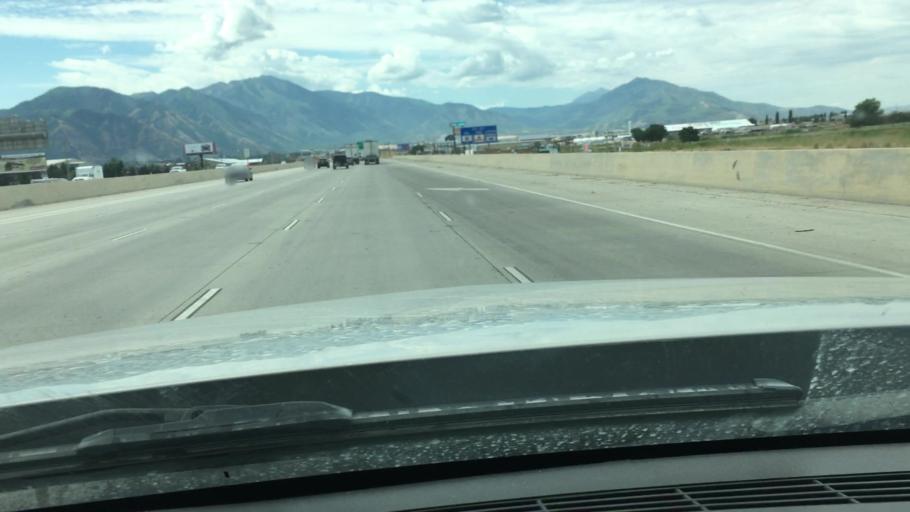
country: US
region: Utah
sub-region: Utah County
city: Springville
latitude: 40.1549
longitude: -111.6474
